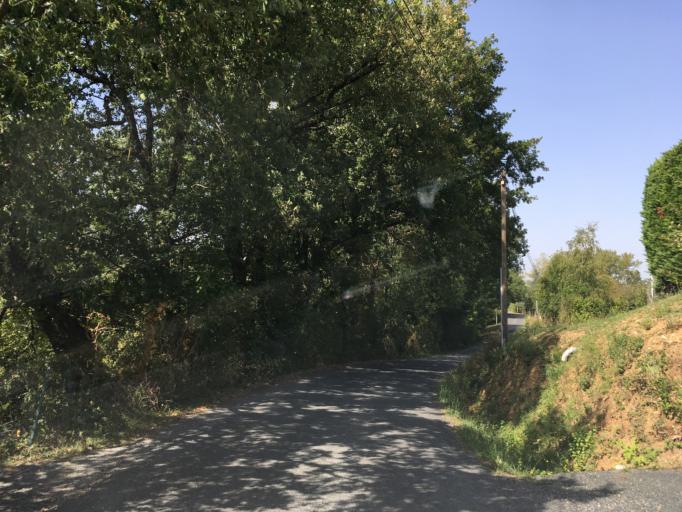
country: FR
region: Midi-Pyrenees
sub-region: Departement du Tarn
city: Castres
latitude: 43.6114
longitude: 2.2790
